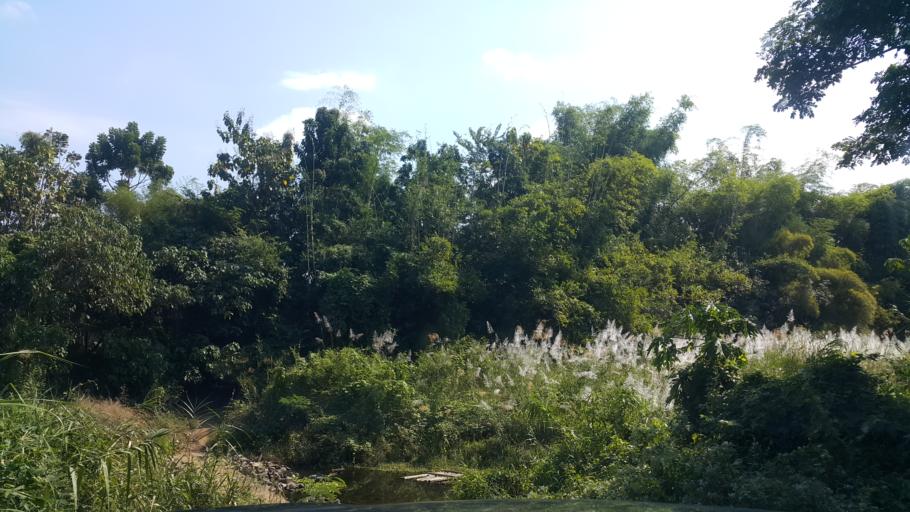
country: TH
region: Sukhothai
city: Thung Saliam
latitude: 17.3238
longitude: 99.5809
